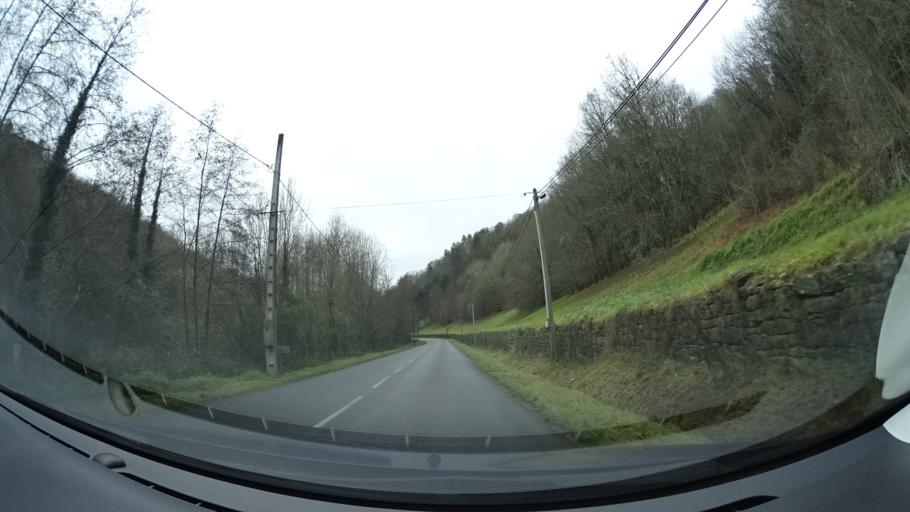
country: FR
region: Aquitaine
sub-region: Departement de la Dordogne
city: Saint-Cyprien
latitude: 44.8836
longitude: 1.0663
